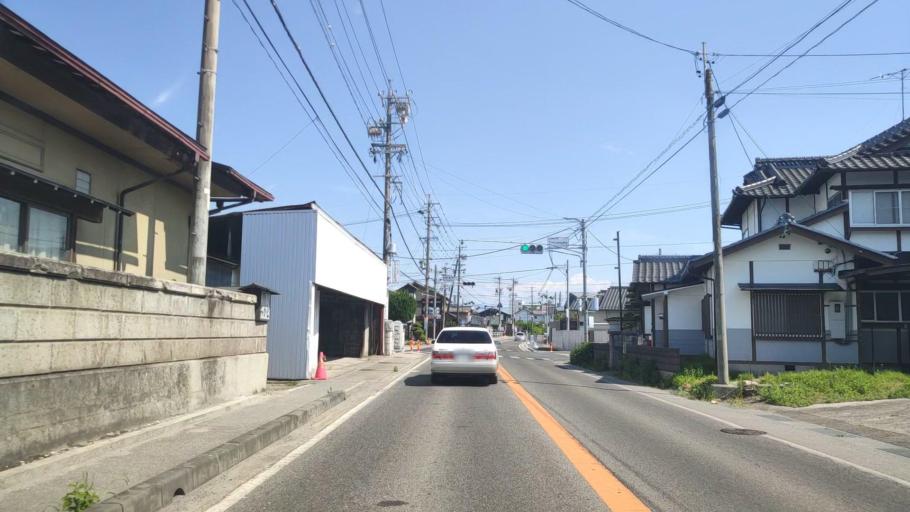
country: JP
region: Nagano
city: Hotaka
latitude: 36.3456
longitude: 137.8855
